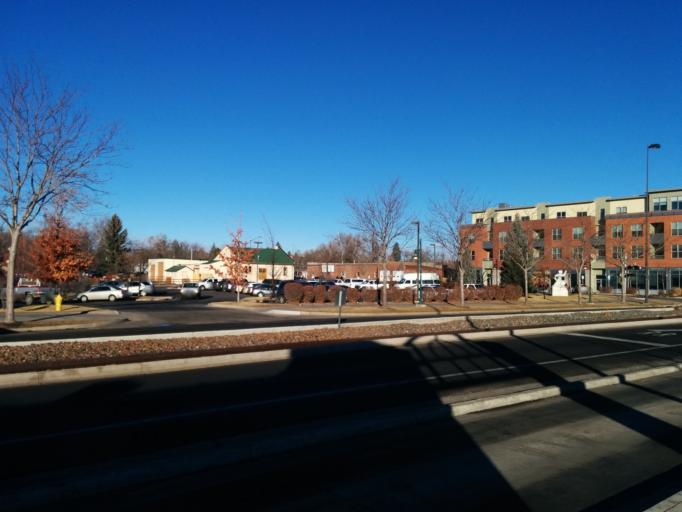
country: US
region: Colorado
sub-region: Larimer County
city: Fort Collins
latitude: 40.5900
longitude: -105.0787
